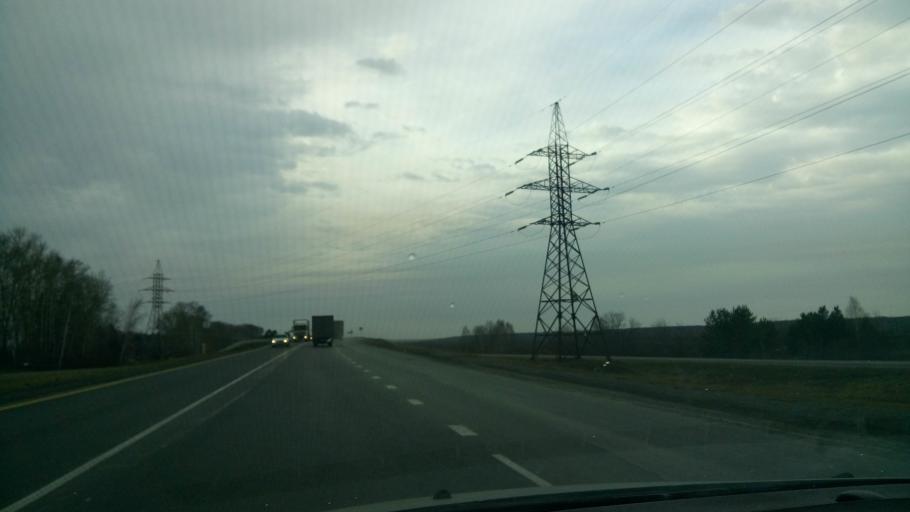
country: RU
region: Sverdlovsk
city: Obukhovskoye
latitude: 56.8426
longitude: 62.5881
